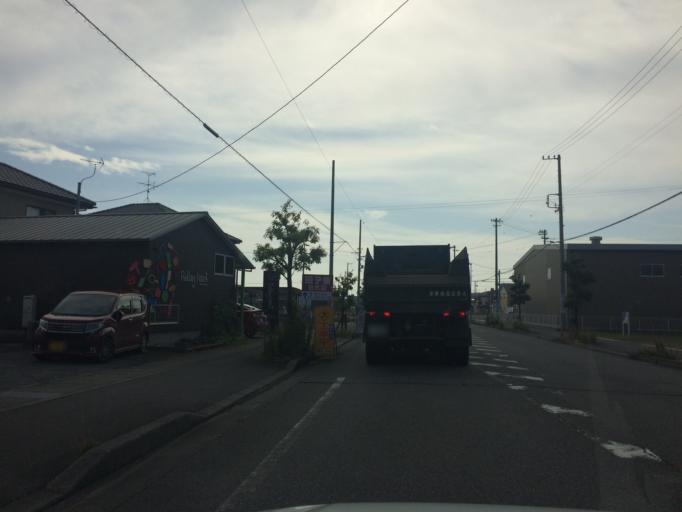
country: JP
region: Shizuoka
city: Yaizu
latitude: 34.8412
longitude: 138.3176
